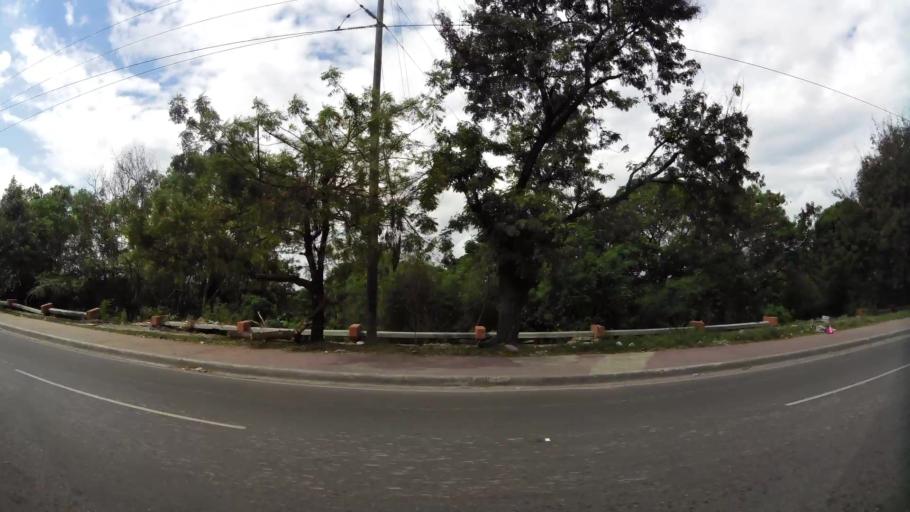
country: DO
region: Santiago
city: Santiago de los Caballeros
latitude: 19.4700
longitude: -70.7164
